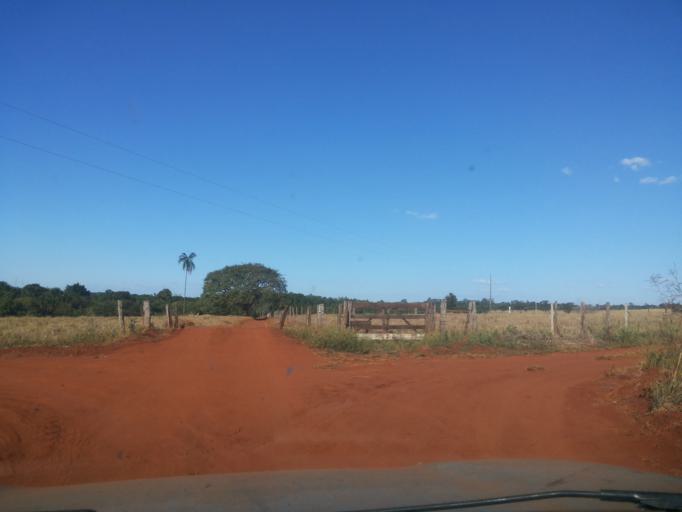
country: BR
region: Minas Gerais
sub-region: Centralina
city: Centralina
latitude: -18.7397
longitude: -49.1628
